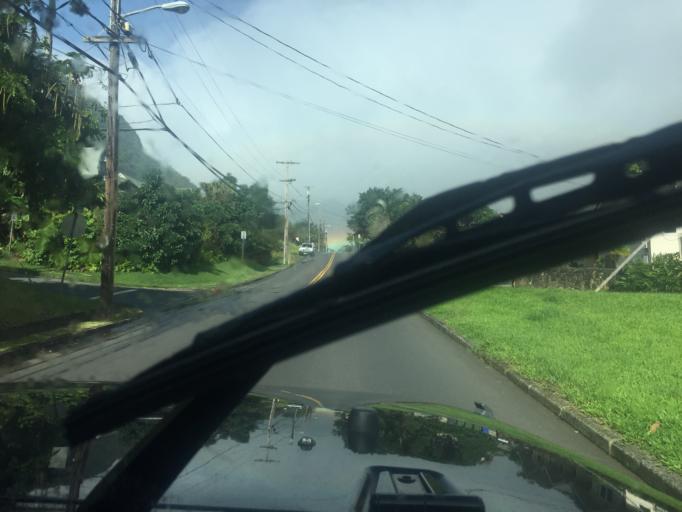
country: US
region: Hawaii
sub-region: Honolulu County
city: Honolulu
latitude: 21.3166
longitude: -157.8112
